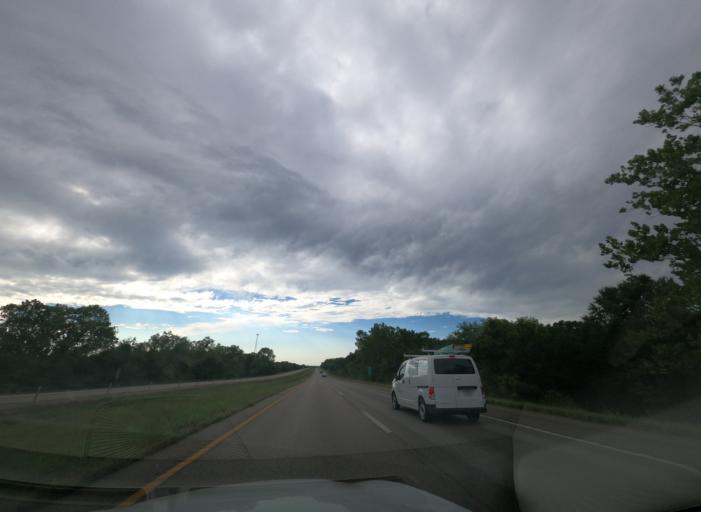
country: US
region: Missouri
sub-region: Sainte Genevieve County
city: Sainte Genevieve
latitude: 37.9600
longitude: -90.1656
